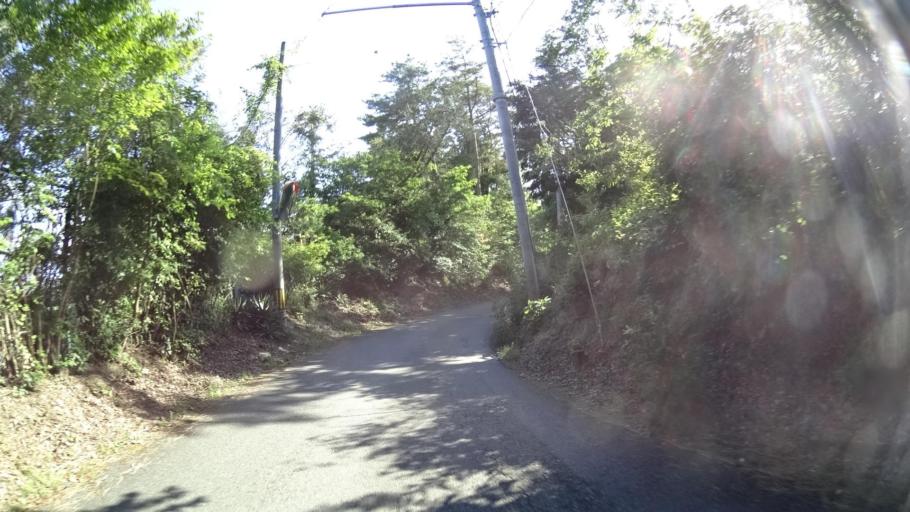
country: JP
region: Kyoto
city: Kameoka
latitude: 34.9857
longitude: 135.5586
